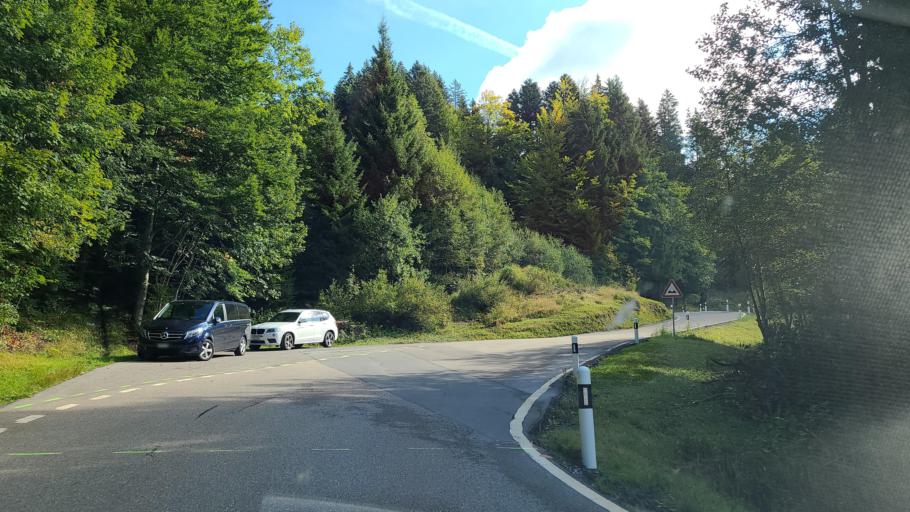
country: CH
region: Schwyz
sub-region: Bezirk March
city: Altendorf
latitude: 47.1304
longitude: 8.8299
